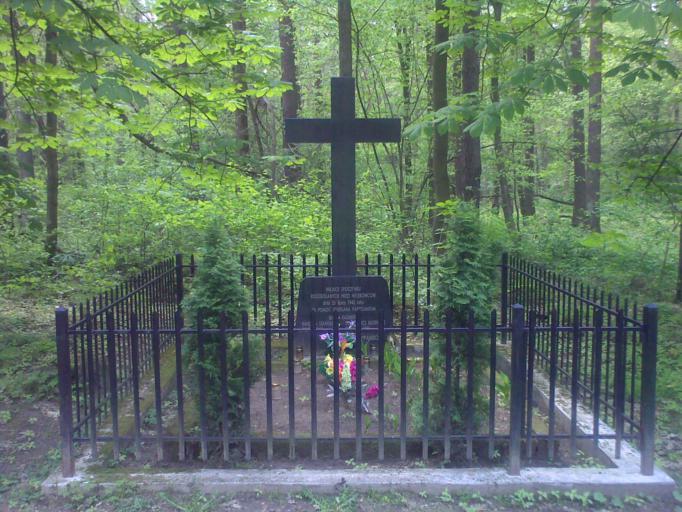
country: PL
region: Masovian Voivodeship
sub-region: Powiat piaseczynski
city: Tarczyn
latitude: 51.9599
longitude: 20.8073
